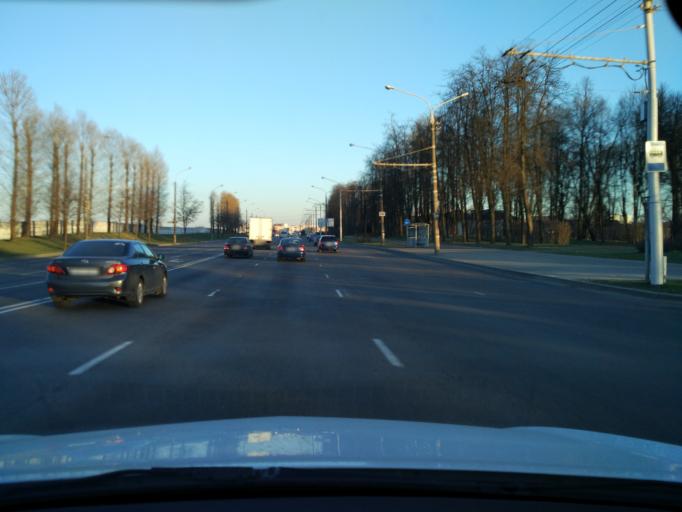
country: BY
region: Minsk
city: Syenitsa
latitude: 53.8653
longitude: 27.5296
